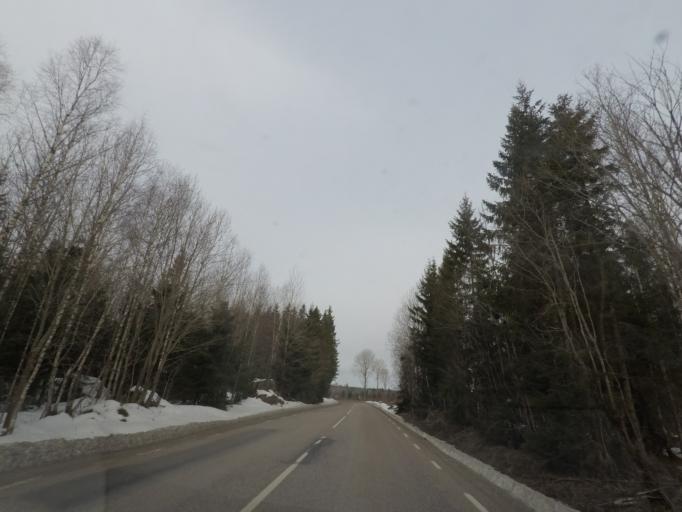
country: SE
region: Vaestmanland
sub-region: Vasteras
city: Skultuna
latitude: 59.7469
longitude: 16.3552
